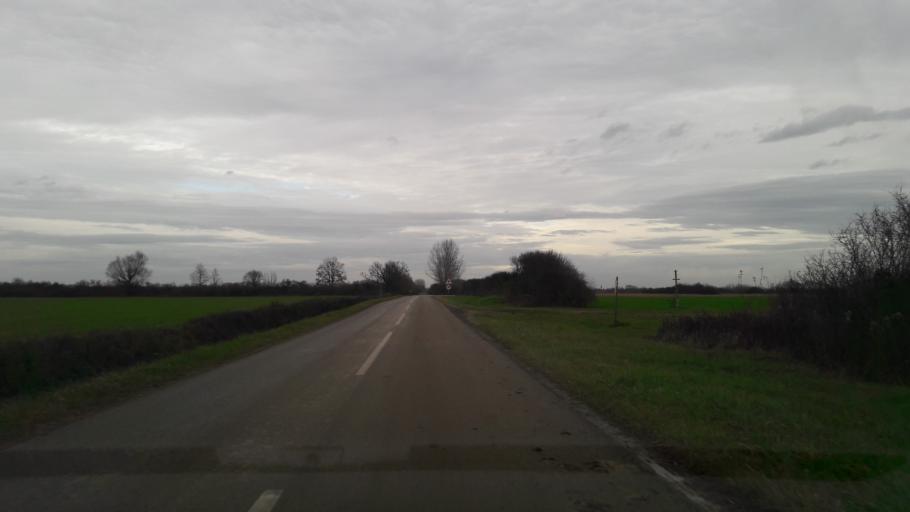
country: HR
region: Osjecko-Baranjska
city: Jelisavac
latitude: 45.6368
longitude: 18.1261
